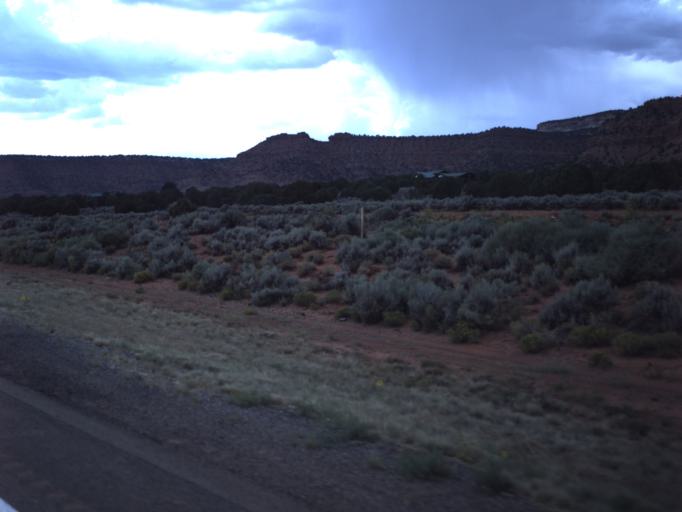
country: US
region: Utah
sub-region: Kane County
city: Kanab
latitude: 37.0305
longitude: -112.4015
